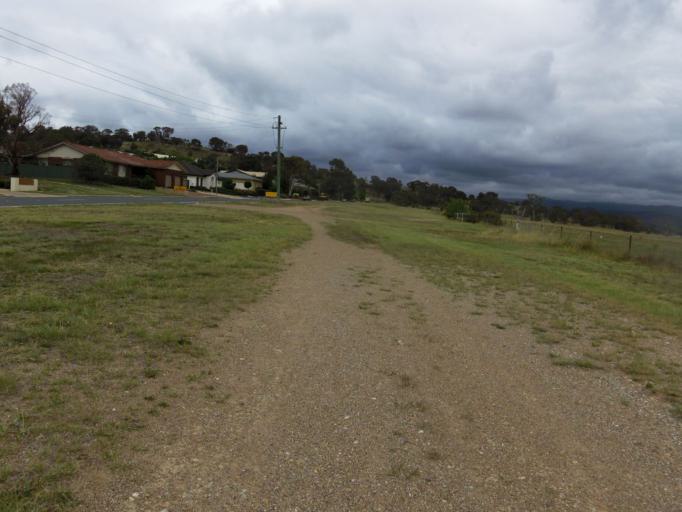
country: AU
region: Australian Capital Territory
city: Macquarie
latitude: -35.3470
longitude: 149.0266
